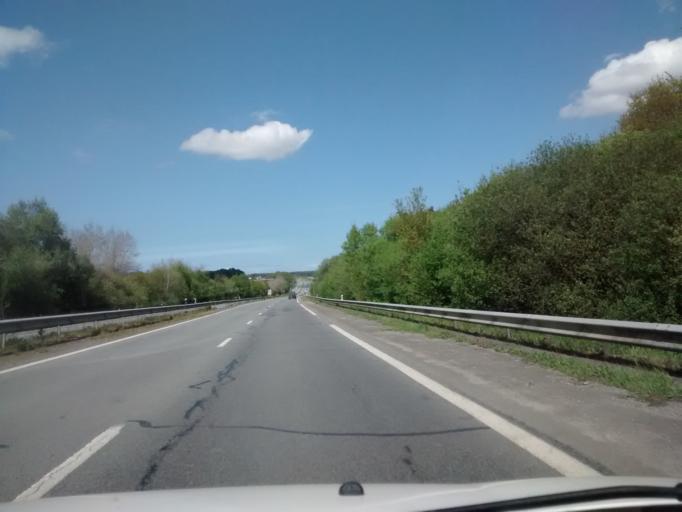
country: FR
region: Brittany
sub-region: Departement des Cotes-d'Armor
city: Saint-Samson-sur-Rance
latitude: 48.4933
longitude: -2.0411
